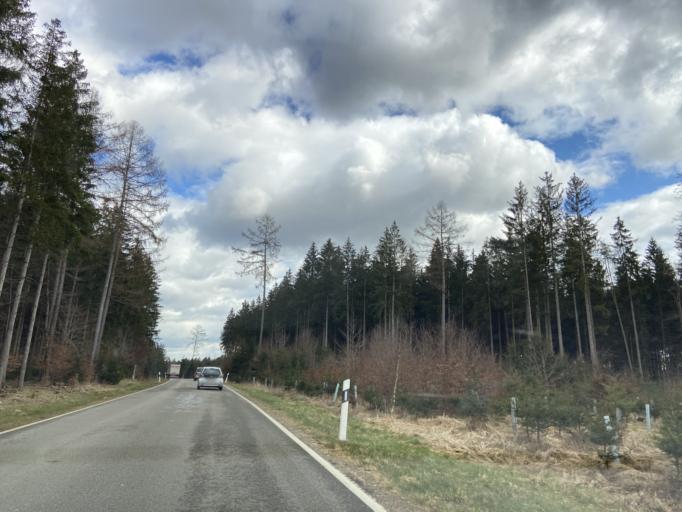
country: DE
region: Baden-Wuerttemberg
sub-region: Tuebingen Region
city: Ostrach
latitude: 47.9584
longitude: 9.3453
